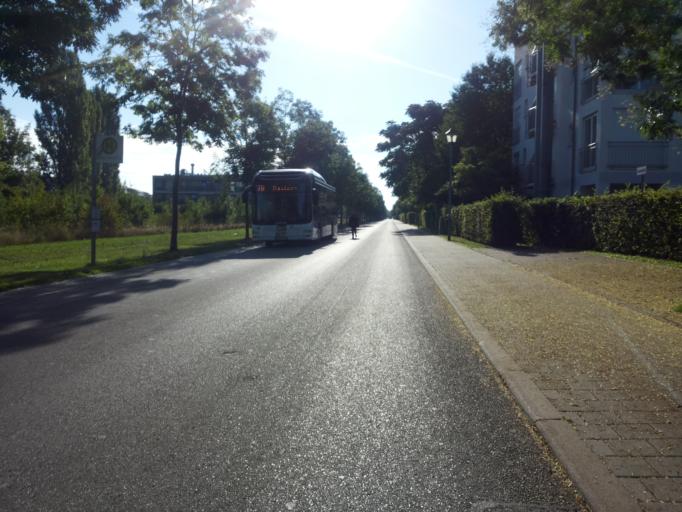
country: DE
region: Bavaria
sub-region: Upper Bavaria
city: Gaimersheim
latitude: 48.7697
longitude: 11.3812
